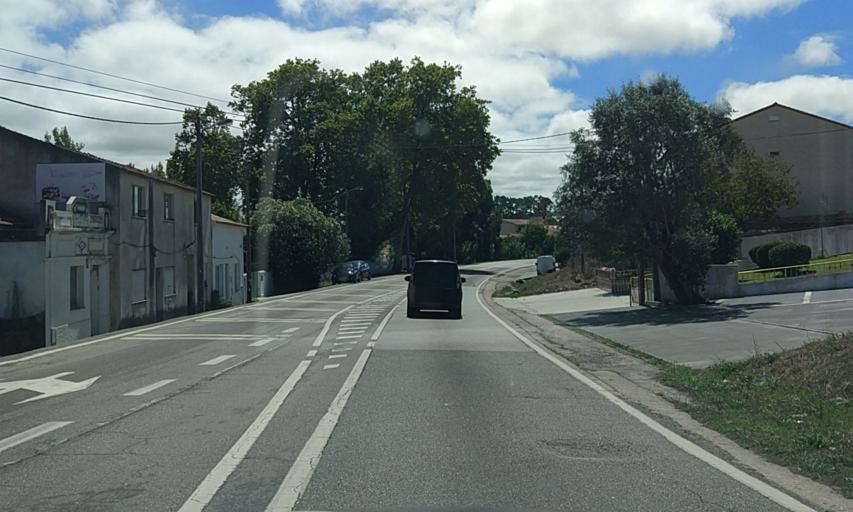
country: PT
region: Aveiro
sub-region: Vagos
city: Vagos
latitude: 40.5109
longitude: -8.6773
